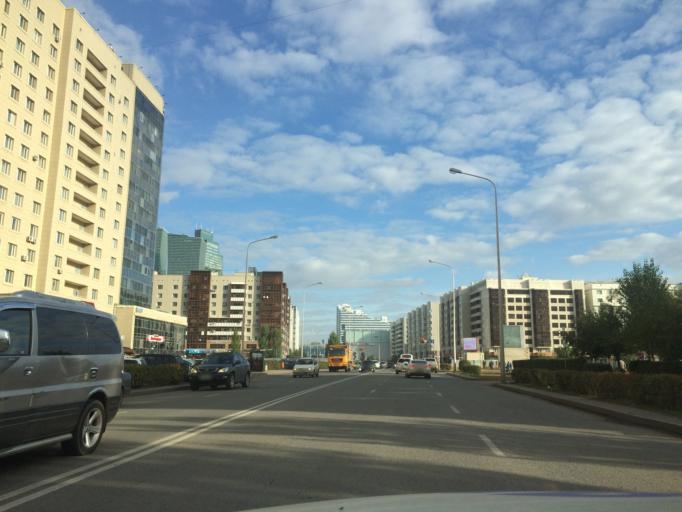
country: KZ
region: Astana Qalasy
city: Astana
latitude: 51.1226
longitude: 71.4220
